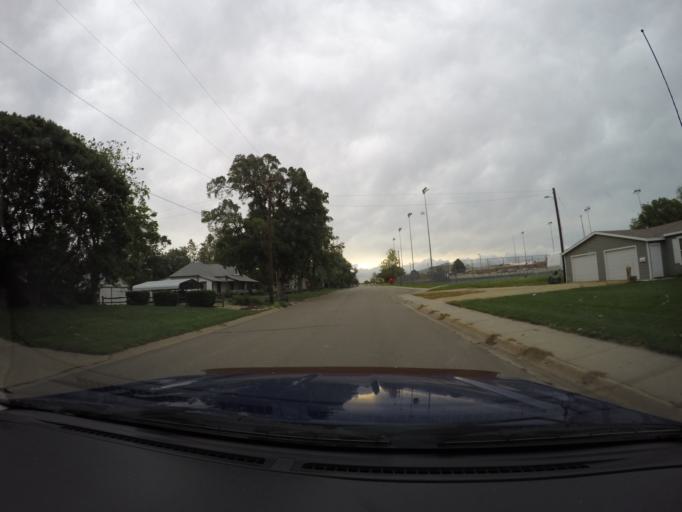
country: US
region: Kansas
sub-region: Clay County
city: Clay Center
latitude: 39.3838
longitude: -97.1190
